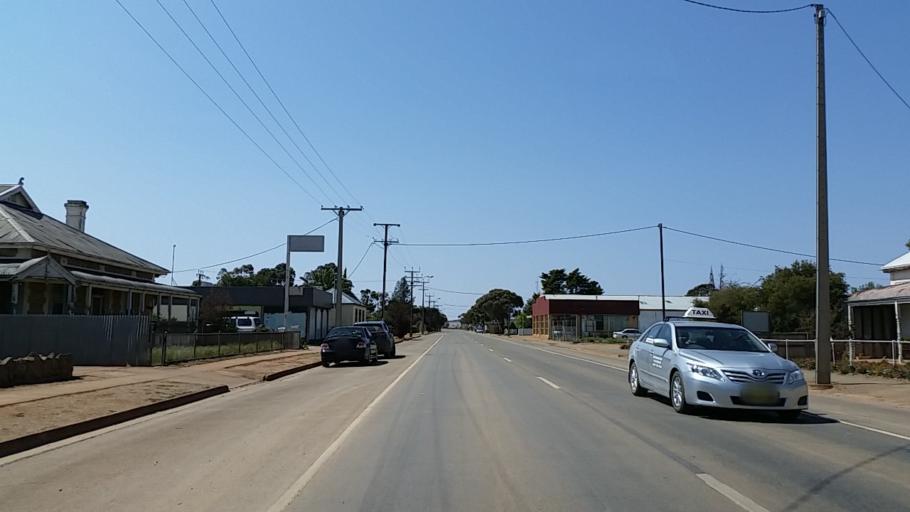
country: AU
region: South Australia
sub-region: Peterborough
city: Peterborough
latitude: -32.9729
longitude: 138.8425
